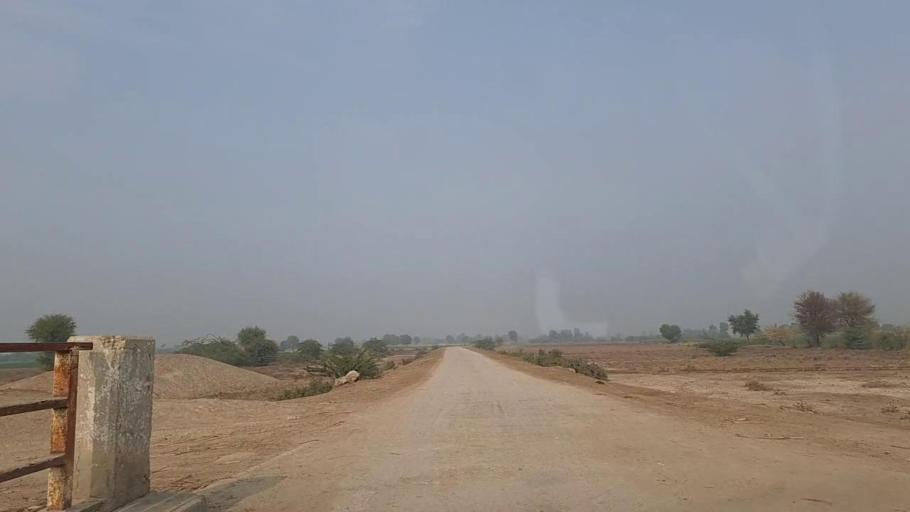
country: PK
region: Sindh
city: Sanghar
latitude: 26.0900
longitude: 68.8977
